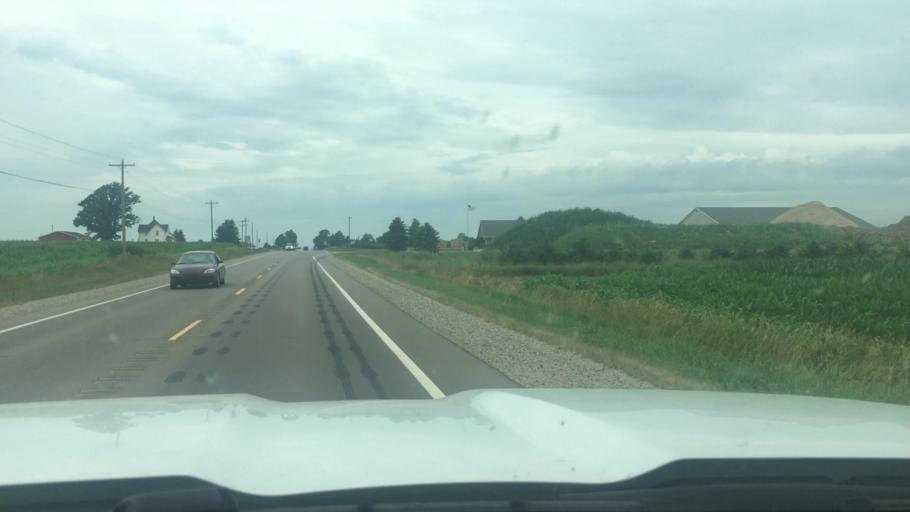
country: US
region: Michigan
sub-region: Clinton County
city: Fowler
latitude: 43.0017
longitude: -84.6964
